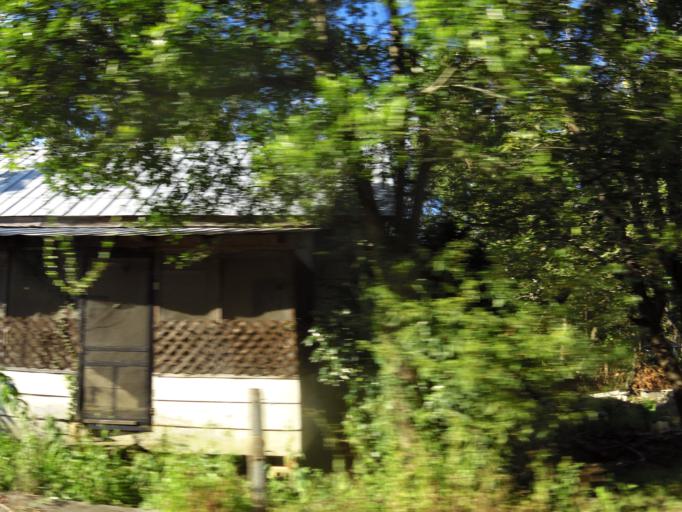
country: US
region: Georgia
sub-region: Brooks County
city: Quitman
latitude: 30.7763
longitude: -83.5622
